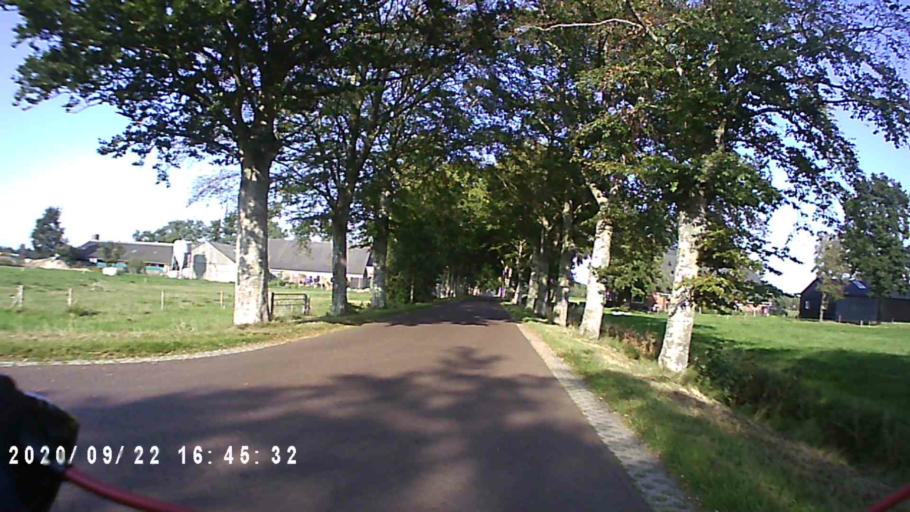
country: NL
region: Groningen
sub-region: Gemeente Leek
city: Leek
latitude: 53.1264
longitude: 6.4677
